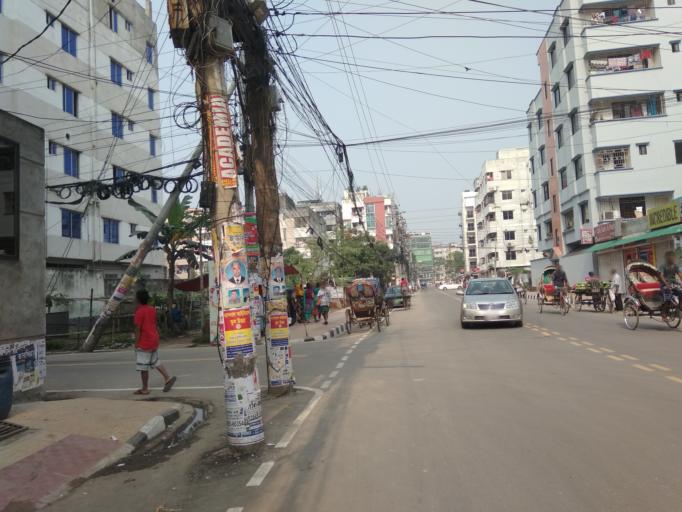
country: BD
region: Dhaka
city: Tungi
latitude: 23.8670
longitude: 90.3856
